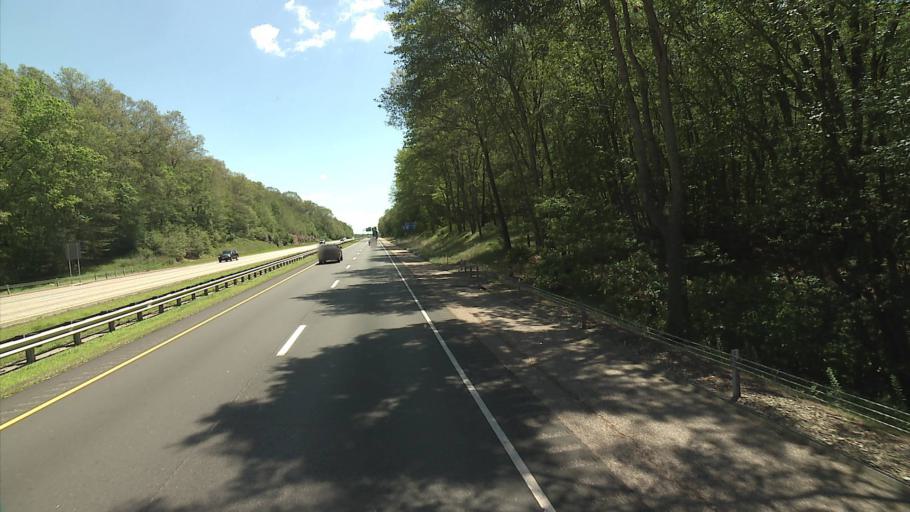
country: US
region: Connecticut
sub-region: New London County
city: Lisbon
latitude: 41.5896
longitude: -72.0065
